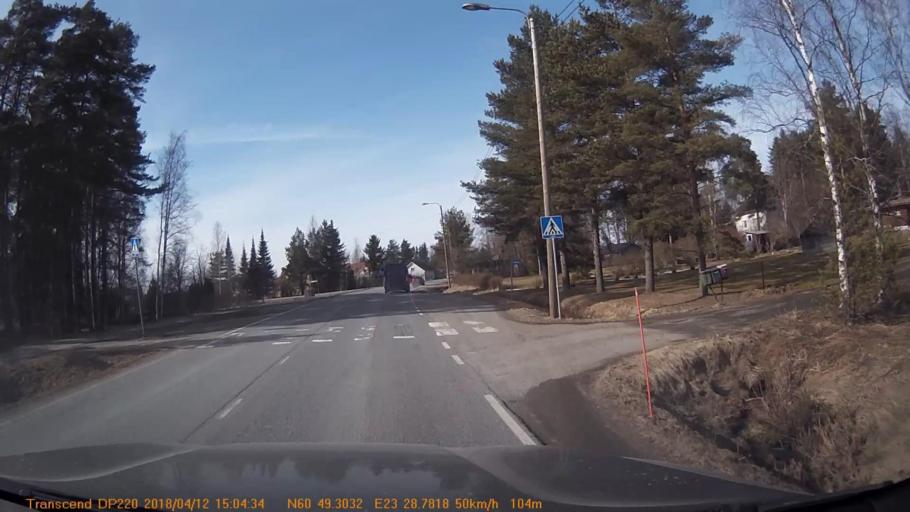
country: FI
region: Haeme
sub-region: Forssa
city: Jokioinen
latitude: 60.8218
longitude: 23.4796
